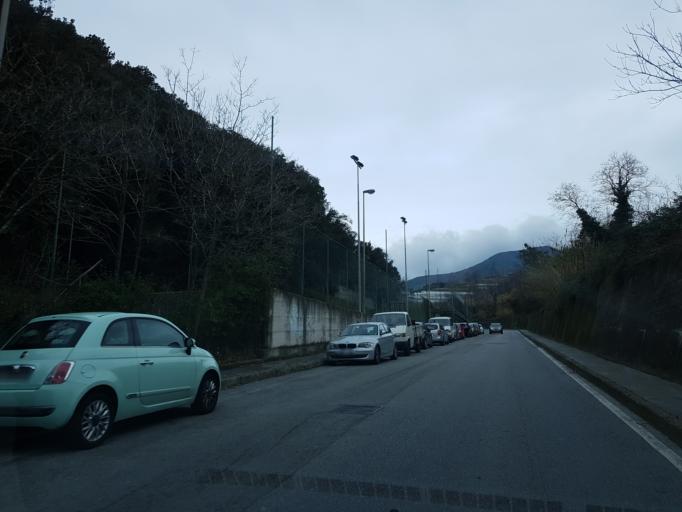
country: IT
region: Liguria
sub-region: Provincia di Genova
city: Mele
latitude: 44.4289
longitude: 8.8012
